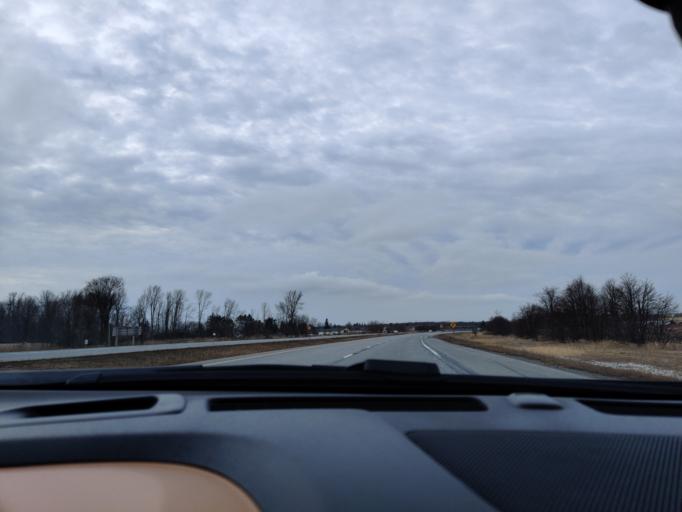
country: CA
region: Ontario
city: Cornwall
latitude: 45.1398
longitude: -74.4913
